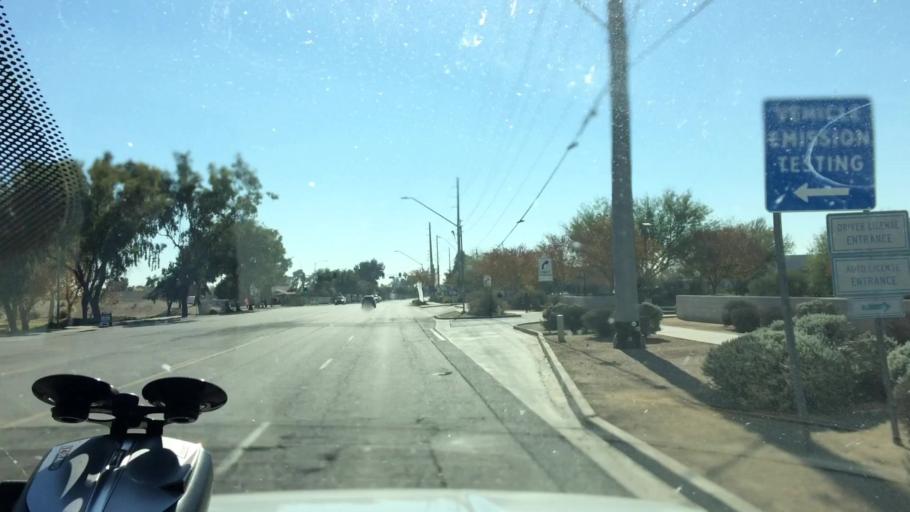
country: US
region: Arizona
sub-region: Maricopa County
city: Peoria
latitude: 33.6340
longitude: -112.1859
